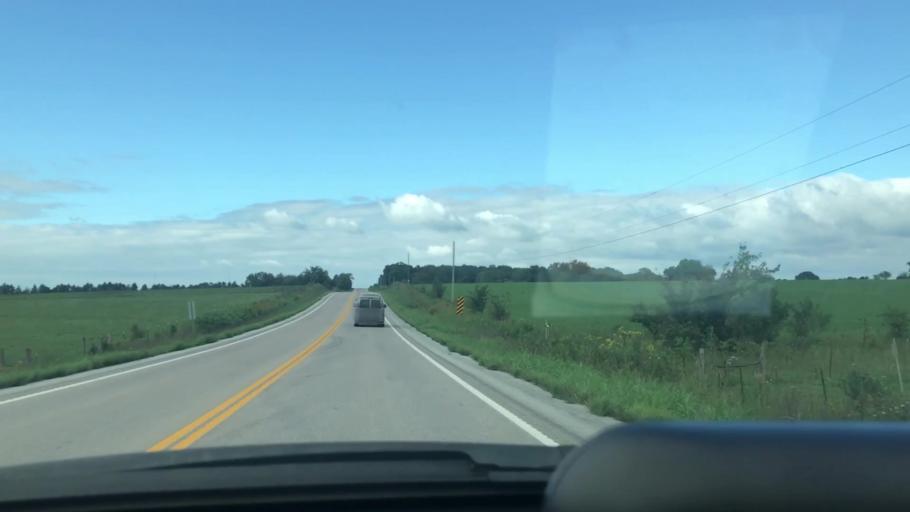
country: US
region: Missouri
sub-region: Hickory County
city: Hermitage
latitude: 37.9572
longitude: -93.2071
